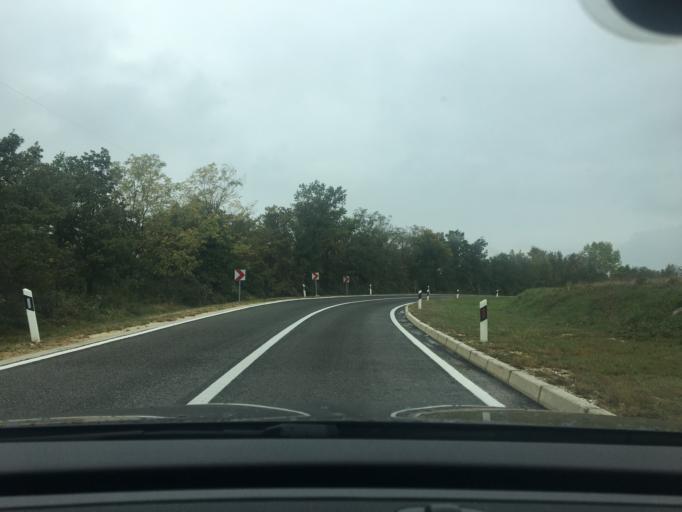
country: HR
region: Istarska
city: Buje
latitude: 45.4285
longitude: 13.6571
